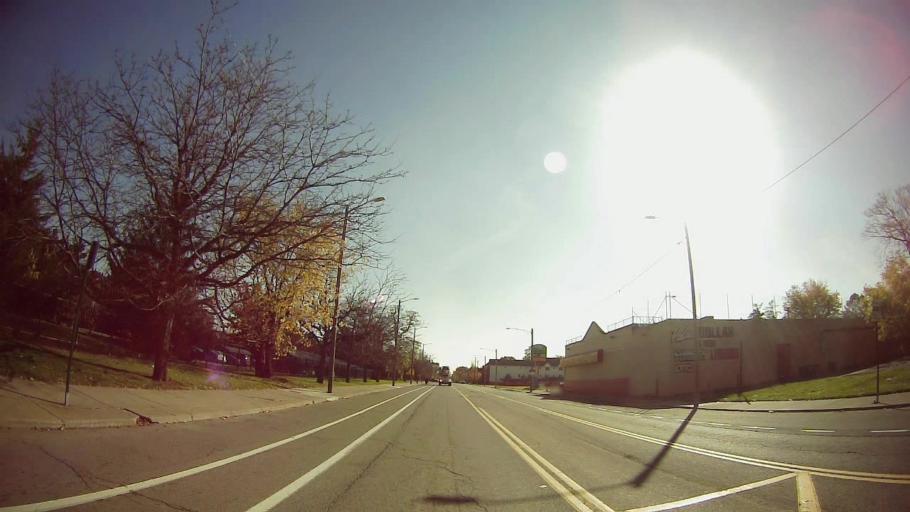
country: US
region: Michigan
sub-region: Wayne County
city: Detroit
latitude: 42.3498
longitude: -83.0773
